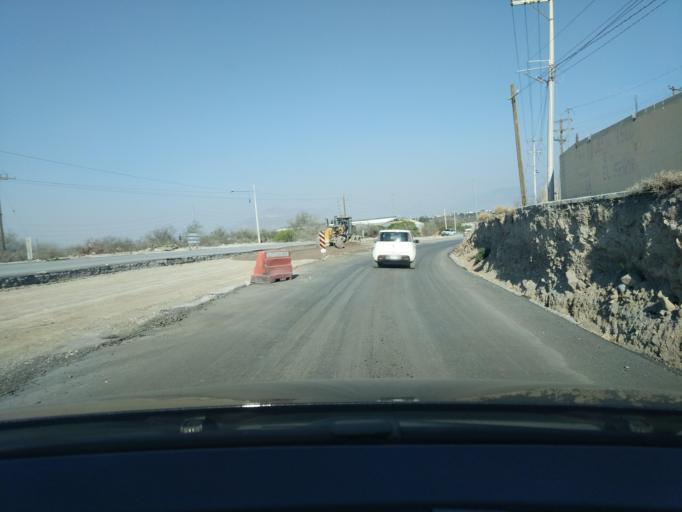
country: MX
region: Coahuila
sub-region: Ramos Arizpe
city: Ramos Arizpe
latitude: 25.5370
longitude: -100.9687
